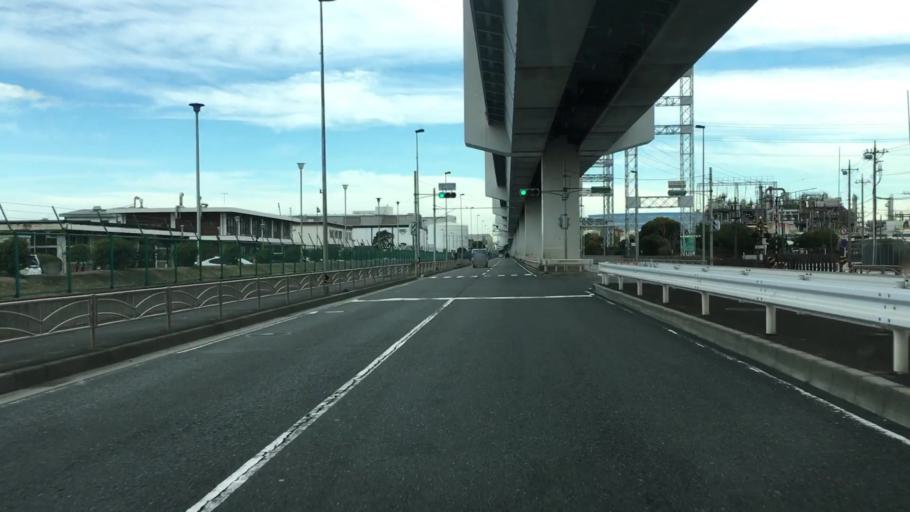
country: JP
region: Kanagawa
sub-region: Kawasaki-shi
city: Kawasaki
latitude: 35.5266
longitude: 139.7776
